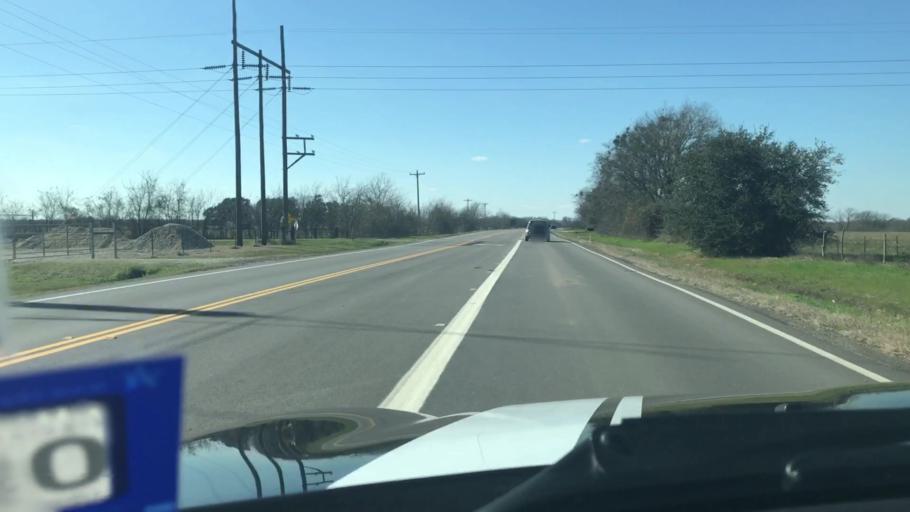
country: US
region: Texas
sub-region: Robertson County
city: Hearne
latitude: 30.8847
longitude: -96.6262
